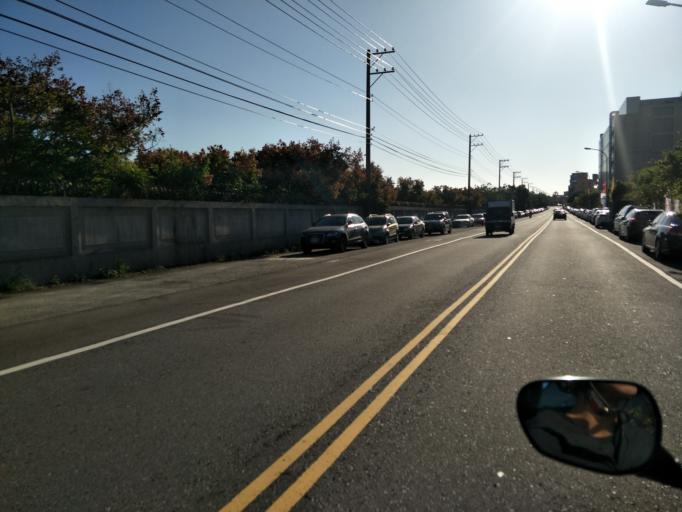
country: TW
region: Taiwan
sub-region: Hsinchu
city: Zhubei
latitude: 24.8732
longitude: 121.0410
